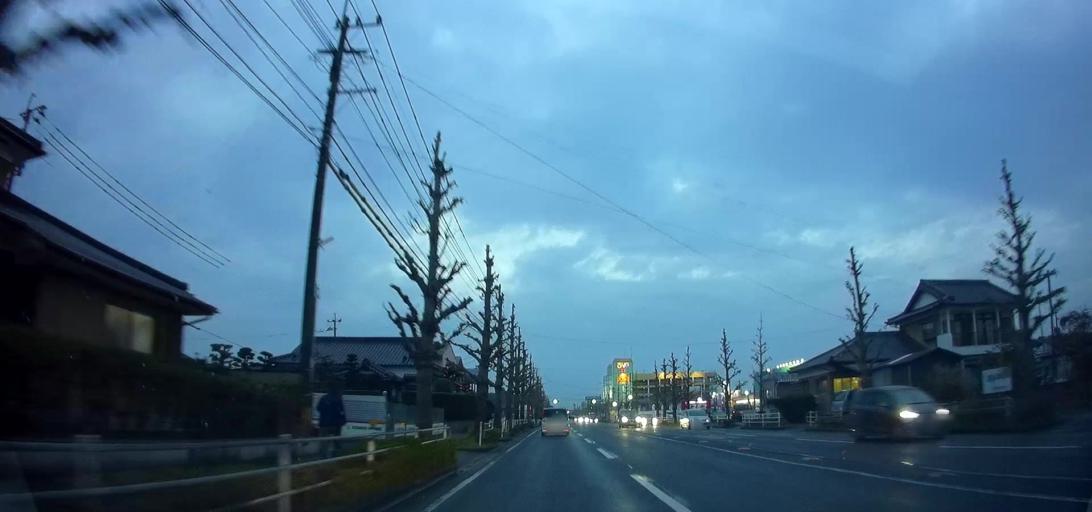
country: JP
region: Nagasaki
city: Omura
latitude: 32.9132
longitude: 129.9479
